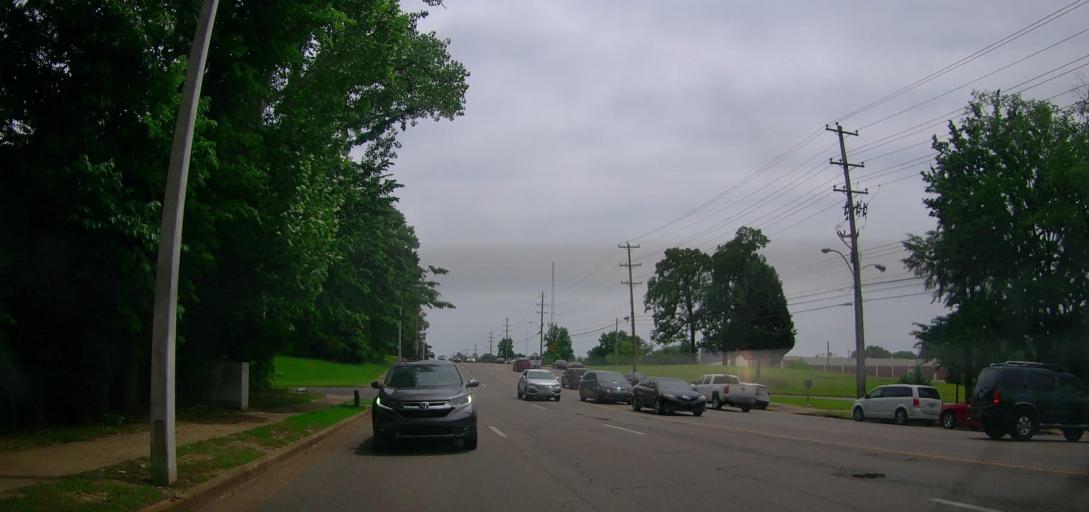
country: US
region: Tennessee
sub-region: Shelby County
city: Germantown
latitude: 35.0909
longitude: -89.8586
